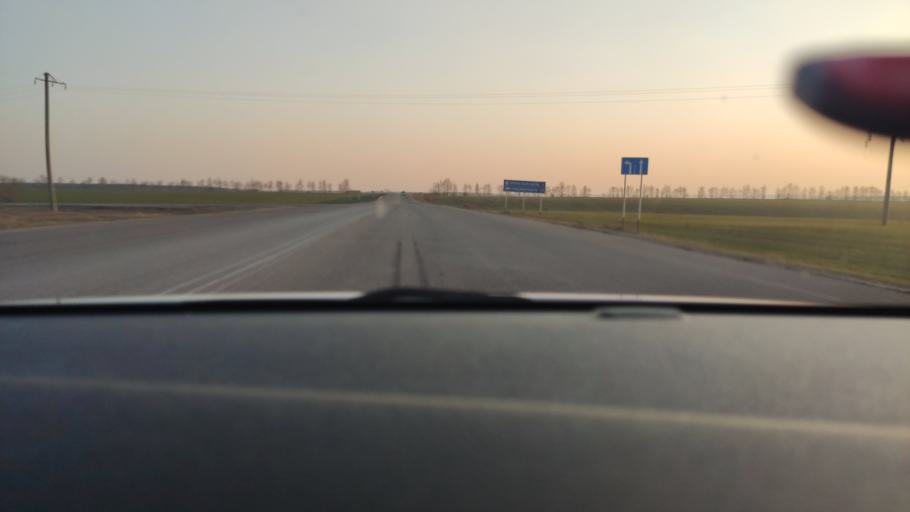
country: RU
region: Voronezj
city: Kolodeznyy
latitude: 51.3985
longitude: 39.2362
